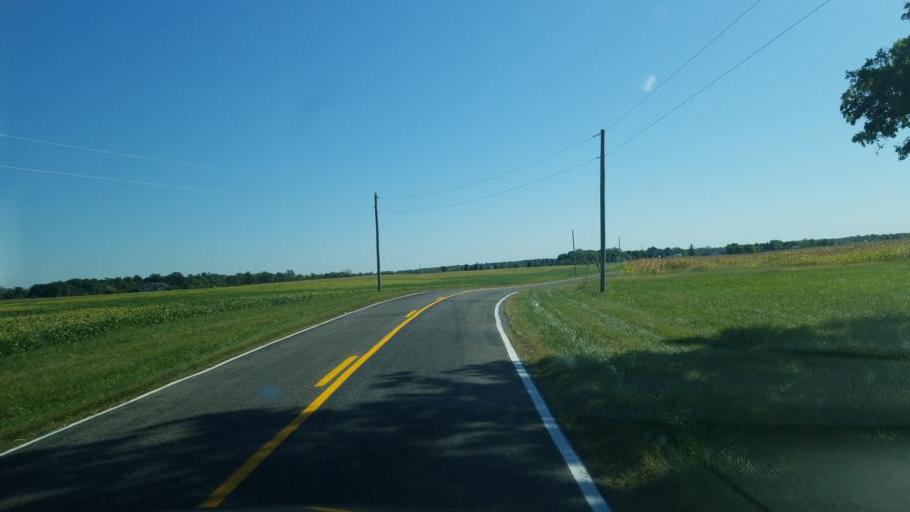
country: US
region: Ohio
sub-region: Champaign County
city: Mechanicsburg
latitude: 40.1357
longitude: -83.5998
